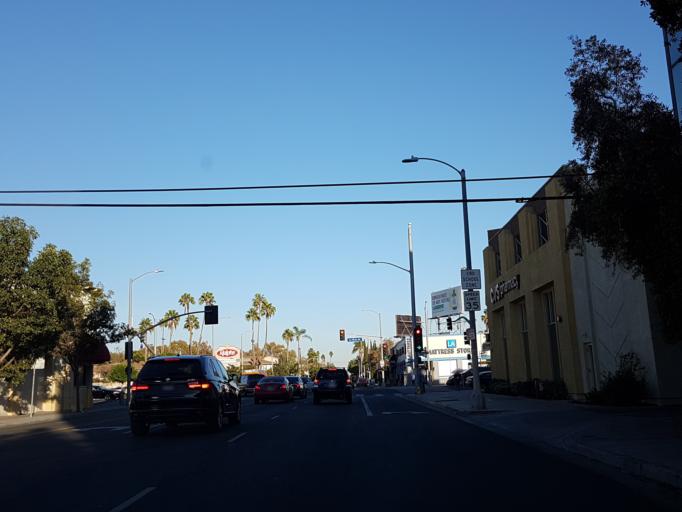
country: US
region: California
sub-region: Los Angeles County
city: West Hollywood
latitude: 34.0688
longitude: -118.3448
